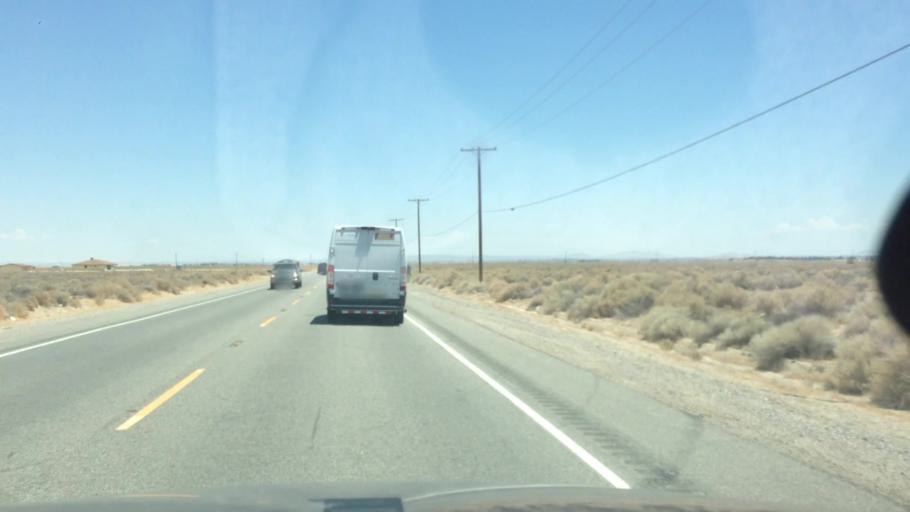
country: US
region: California
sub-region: Kern County
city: Rosamond
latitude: 34.7766
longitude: -118.2107
